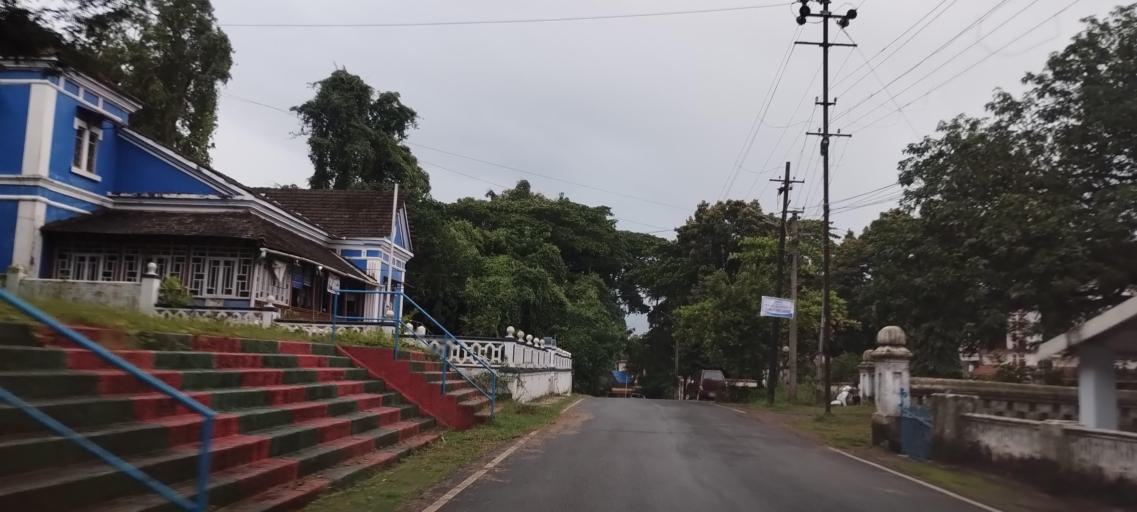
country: IN
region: Goa
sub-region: North Goa
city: Jua
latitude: 15.5257
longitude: 73.9028
